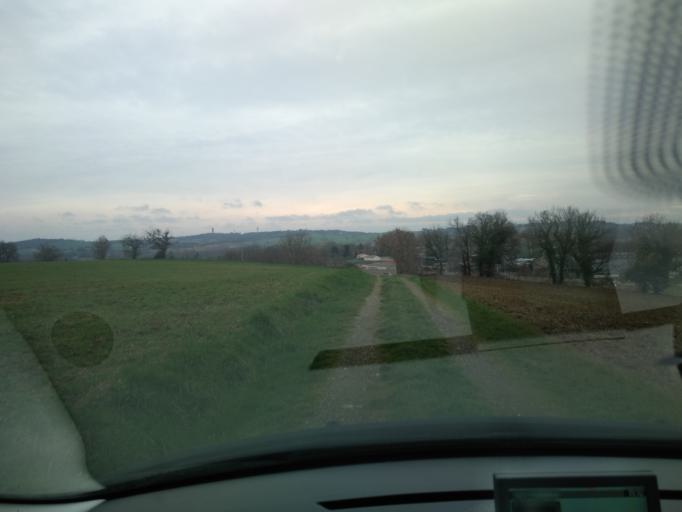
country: FR
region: Midi-Pyrenees
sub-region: Departement de la Haute-Garonne
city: Launac
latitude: 43.7321
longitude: 1.0578
